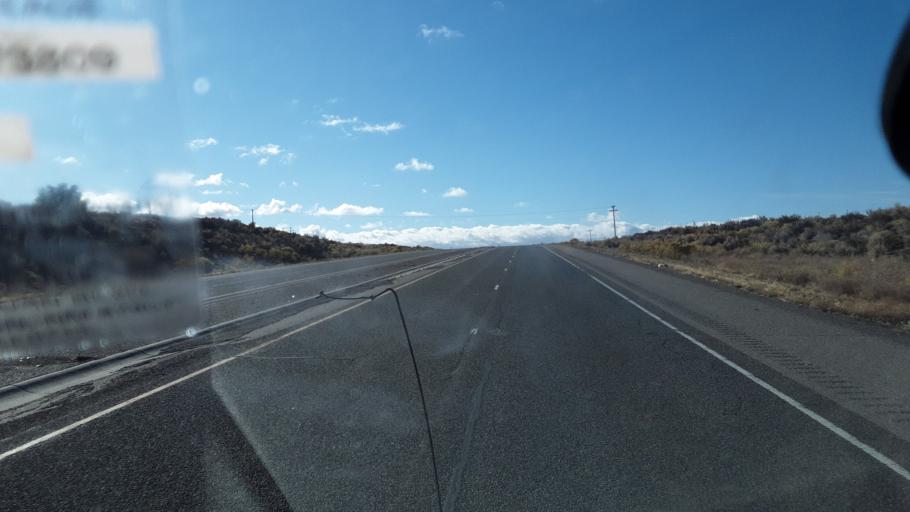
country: US
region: New Mexico
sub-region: San Juan County
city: Lee Acres
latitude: 36.6208
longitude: -108.0170
